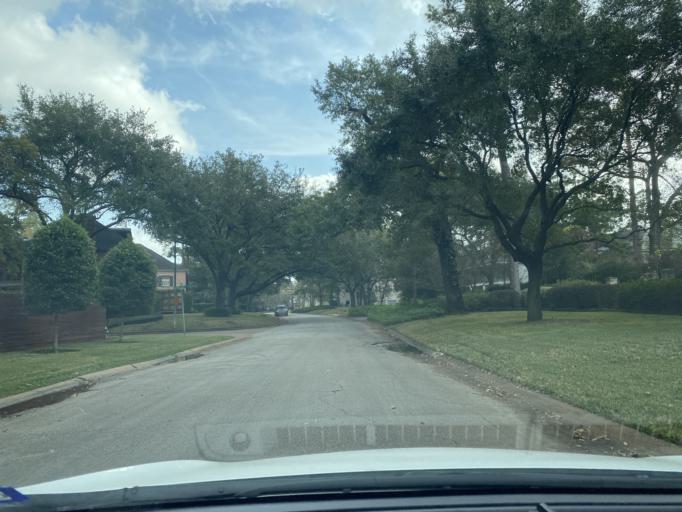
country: US
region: Texas
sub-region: Harris County
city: Hunters Creek Village
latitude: 29.7684
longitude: -95.4700
